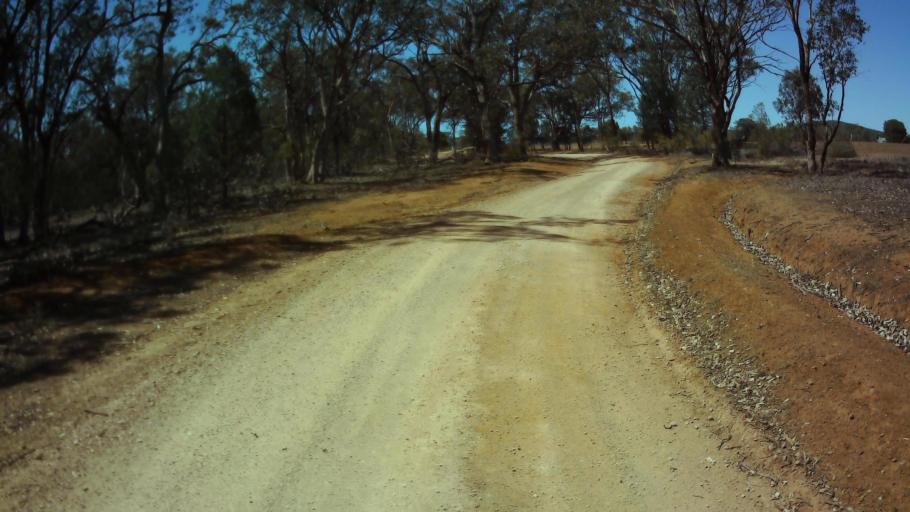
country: AU
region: New South Wales
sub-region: Weddin
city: Grenfell
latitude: -33.9420
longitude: 148.0787
